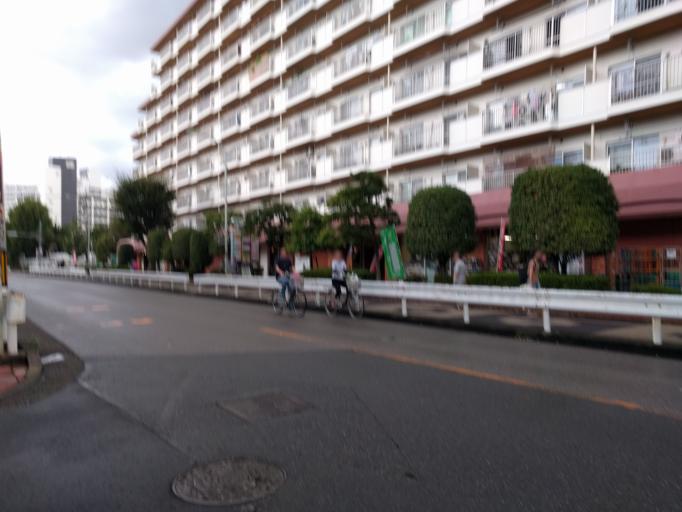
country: JP
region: Saitama
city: Shimotoda
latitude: 35.8299
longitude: 139.6868
